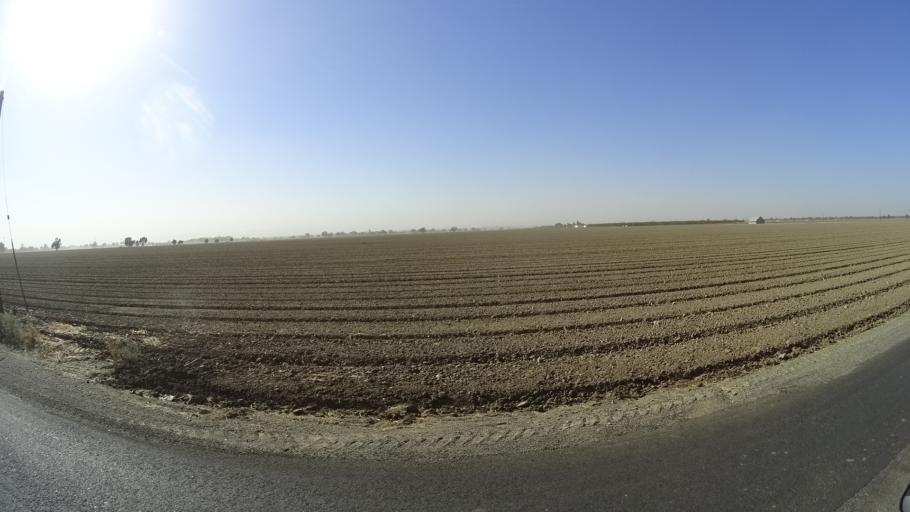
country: US
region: California
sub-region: Yolo County
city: Woodland
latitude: 38.7461
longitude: -121.8027
